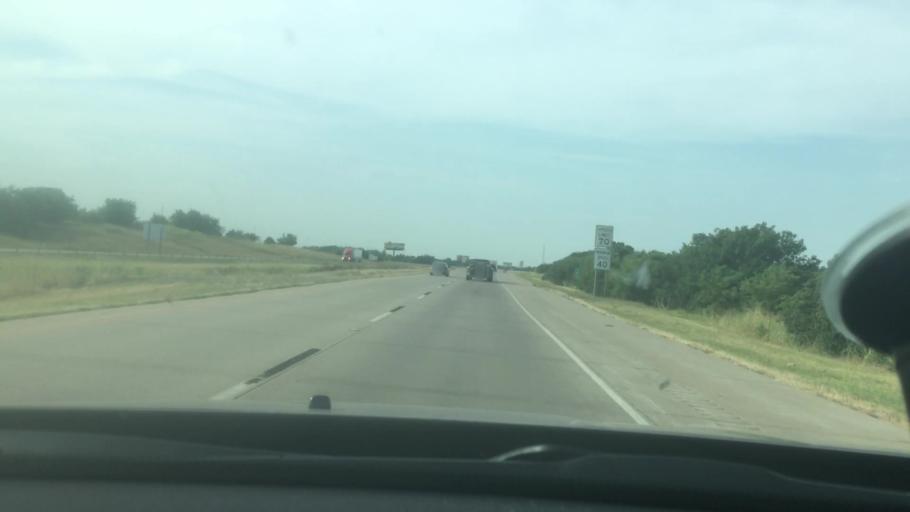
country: US
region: Oklahoma
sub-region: Carter County
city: Ardmore
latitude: 34.2942
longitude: -97.1595
